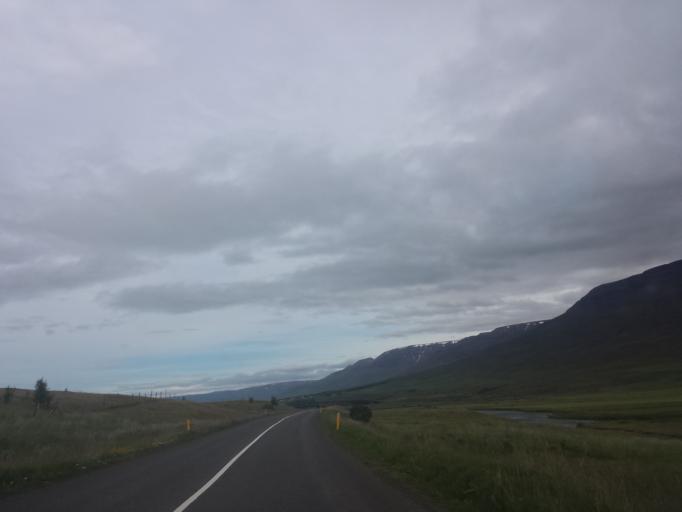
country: IS
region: Northeast
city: Akureyri
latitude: 65.4552
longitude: -18.1968
